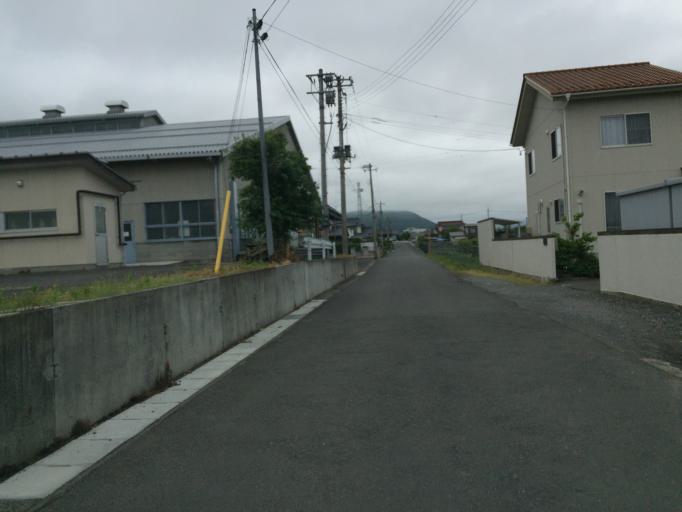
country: JP
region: Fukushima
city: Fukushima-shi
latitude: 37.7715
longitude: 140.3930
